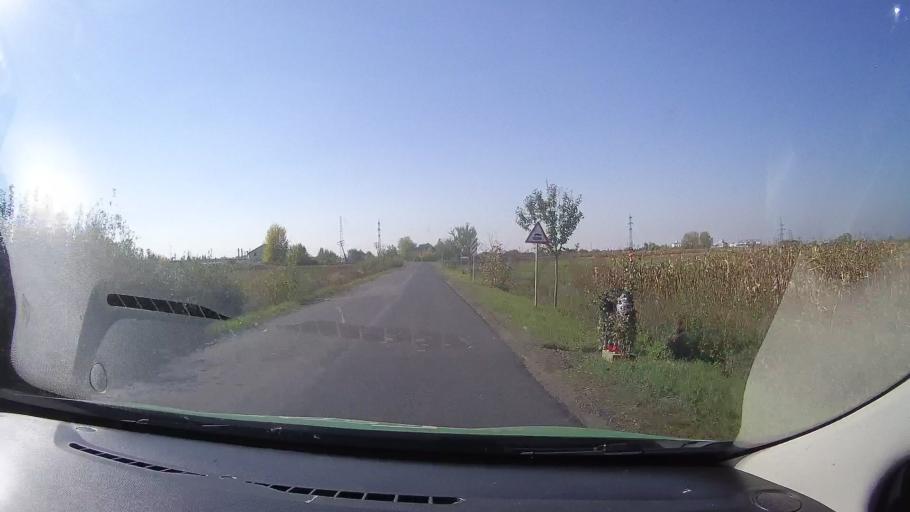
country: RO
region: Satu Mare
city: Carei
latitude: 47.6978
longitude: 22.4837
